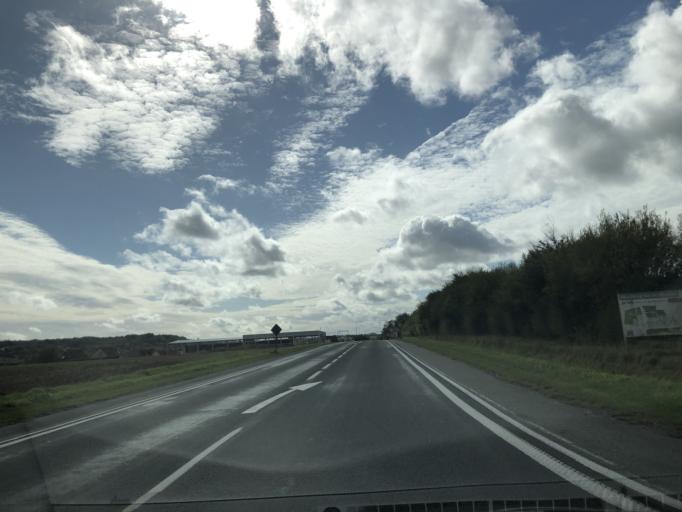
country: FR
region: Nord-Pas-de-Calais
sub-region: Departement du Pas-de-Calais
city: Wizernes
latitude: 50.7179
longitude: 2.2375
